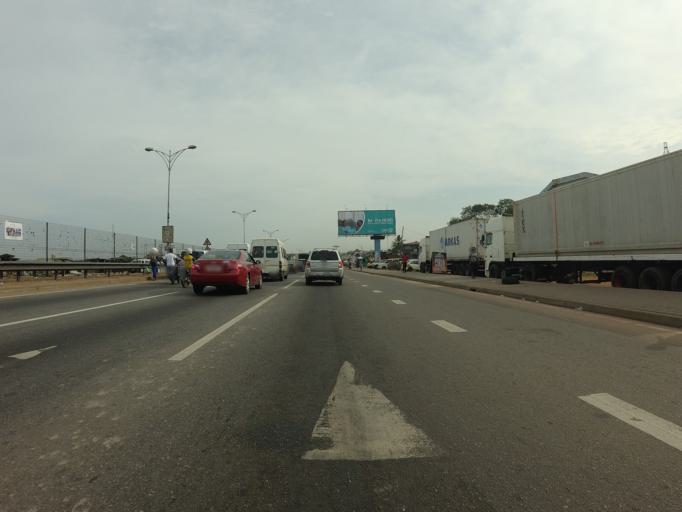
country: GH
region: Greater Accra
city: Gbawe
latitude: 5.5906
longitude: -0.2690
